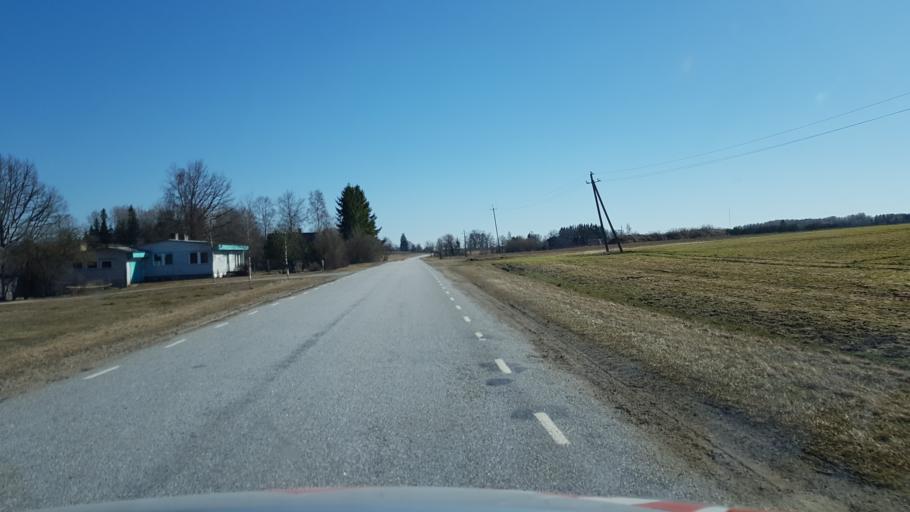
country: EE
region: Jaervamaa
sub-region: Koeru vald
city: Koeru
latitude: 59.0446
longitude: 26.0902
